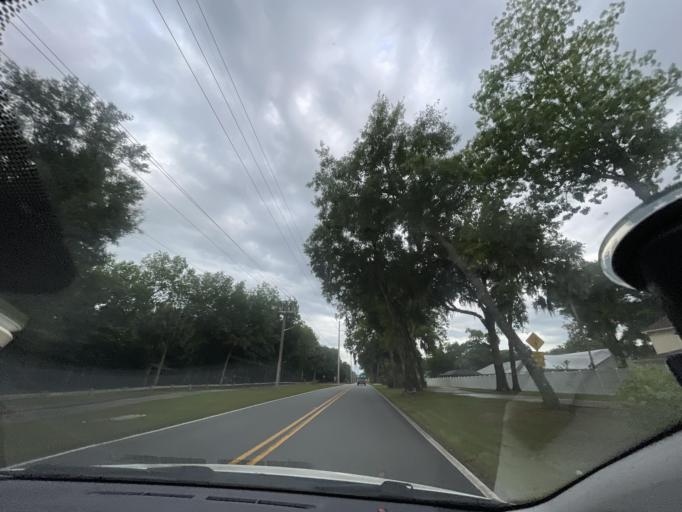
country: US
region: Florida
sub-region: Volusia County
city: Port Orange
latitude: 29.0959
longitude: -80.9931
